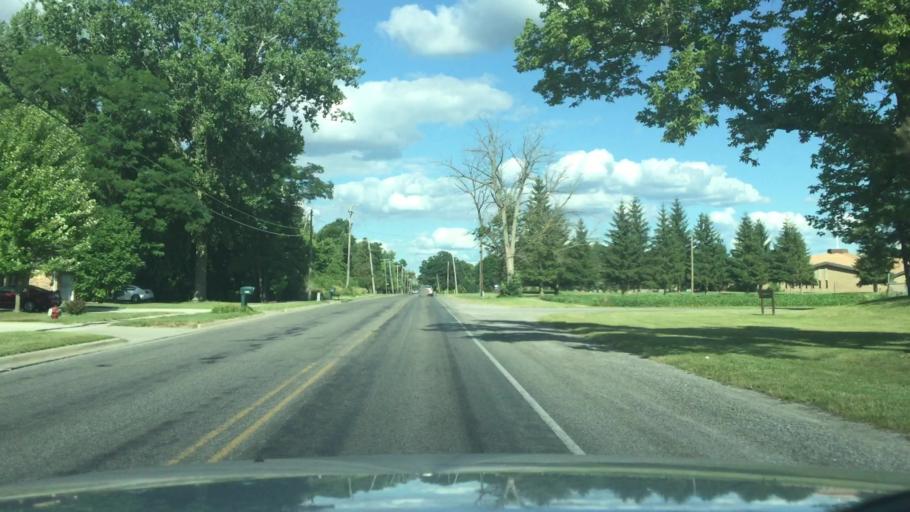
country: US
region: Michigan
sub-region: Saginaw County
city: Shields
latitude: 43.4009
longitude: -84.0123
